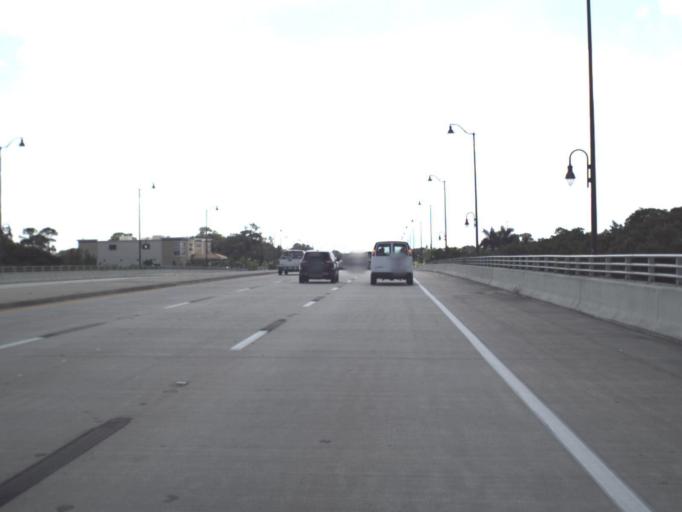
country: US
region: Florida
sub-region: Lee County
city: Bonita Springs
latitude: 26.3397
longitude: -81.8069
